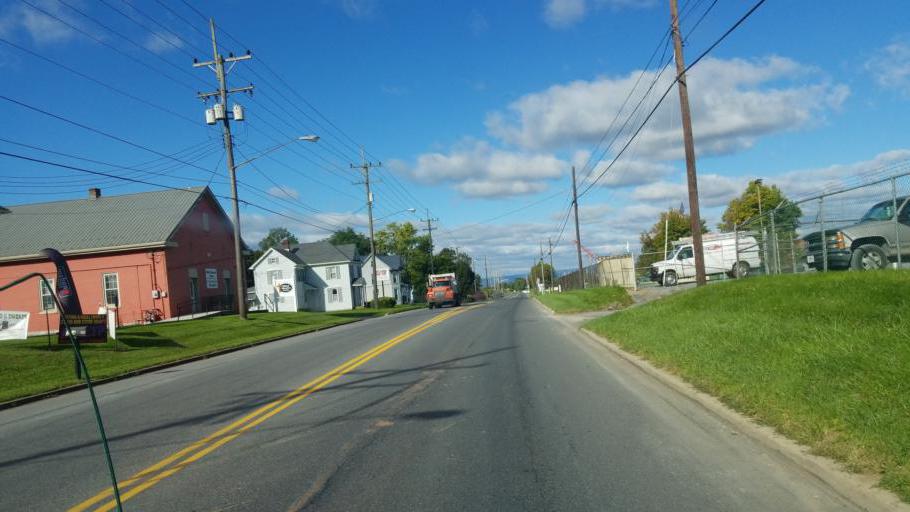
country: US
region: Pennsylvania
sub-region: Franklin County
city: Greencastle
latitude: 39.7799
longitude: -77.6787
